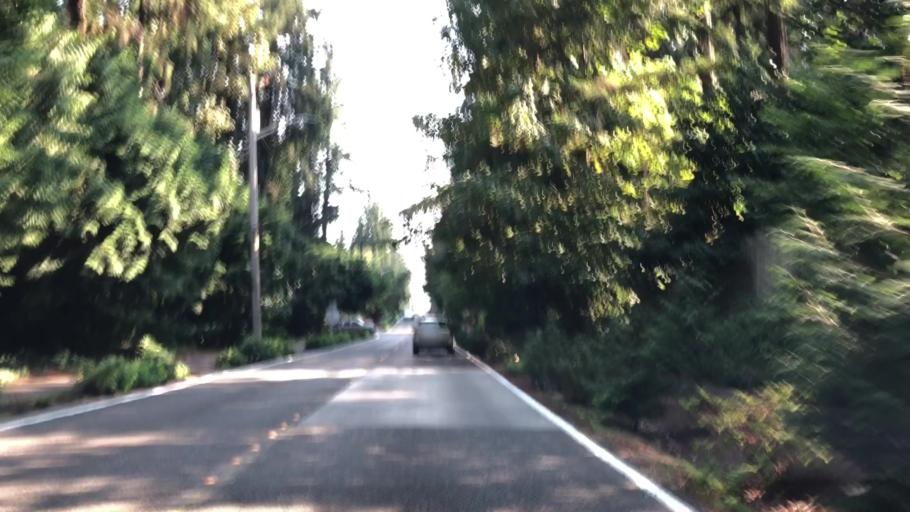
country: US
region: Washington
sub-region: King County
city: Newport
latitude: 47.5865
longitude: -122.1965
